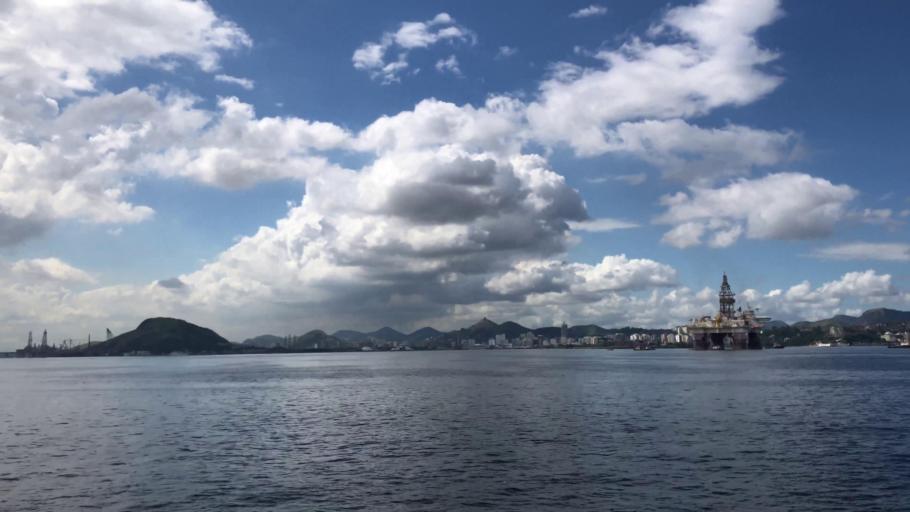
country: BR
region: Rio de Janeiro
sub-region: Niteroi
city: Niteroi
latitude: -22.8966
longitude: -43.1499
